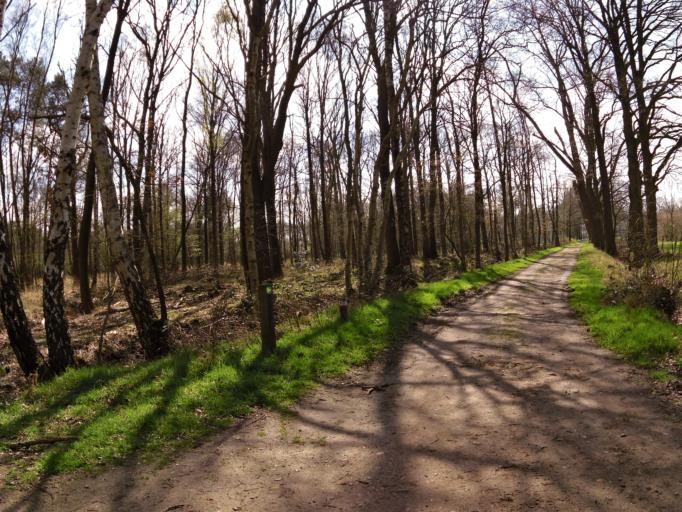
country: NL
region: North Brabant
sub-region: Gemeente Haaren
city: Haaren
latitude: 51.5564
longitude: 5.2660
